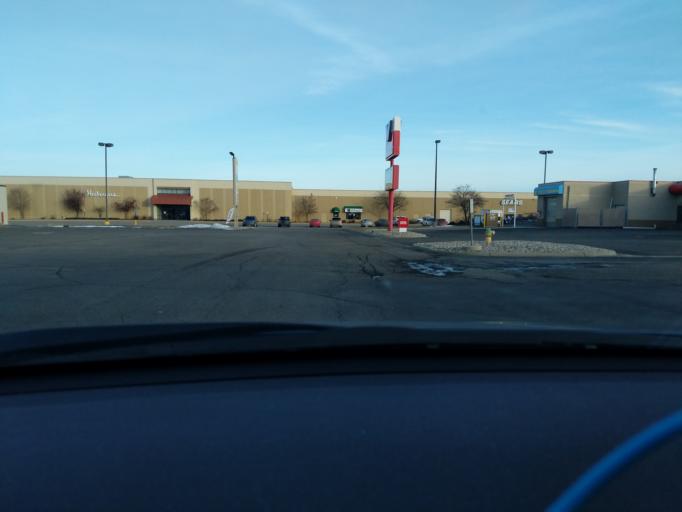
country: US
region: Minnesota
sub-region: Kandiyohi County
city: Willmar
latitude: 45.1075
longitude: -95.0418
